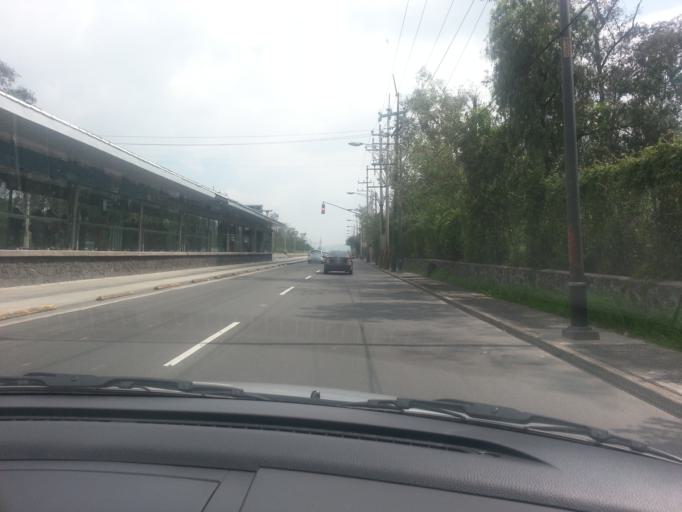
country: MX
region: Mexico City
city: Magdalena Contreras
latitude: 19.3234
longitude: -99.1886
